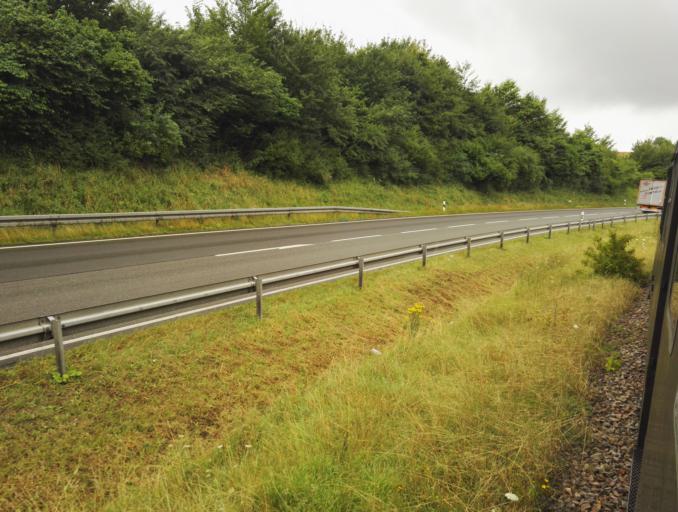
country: DE
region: Baden-Wuerttemberg
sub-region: Freiburg Region
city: Blumberg
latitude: 47.8142
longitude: 8.5541
